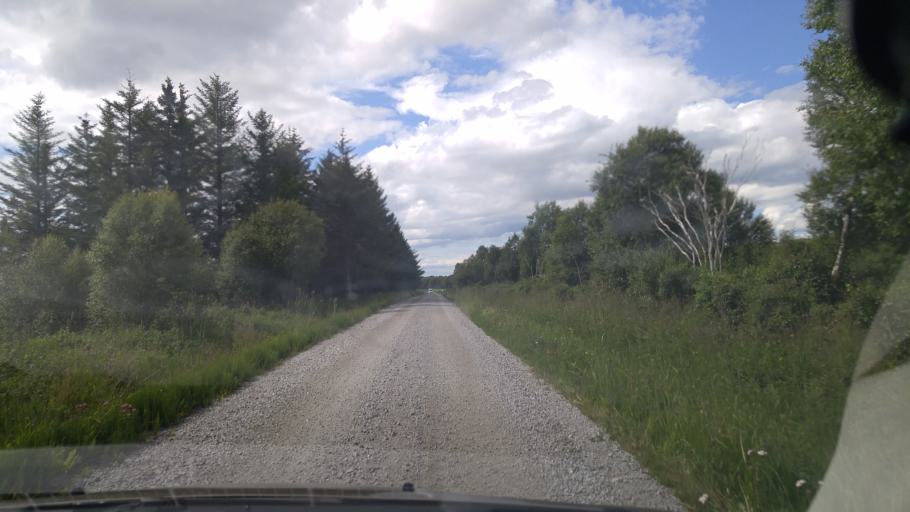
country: NO
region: Nord-Trondelag
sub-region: Vikna
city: Rorvik
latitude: 64.9066
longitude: 11.1310
